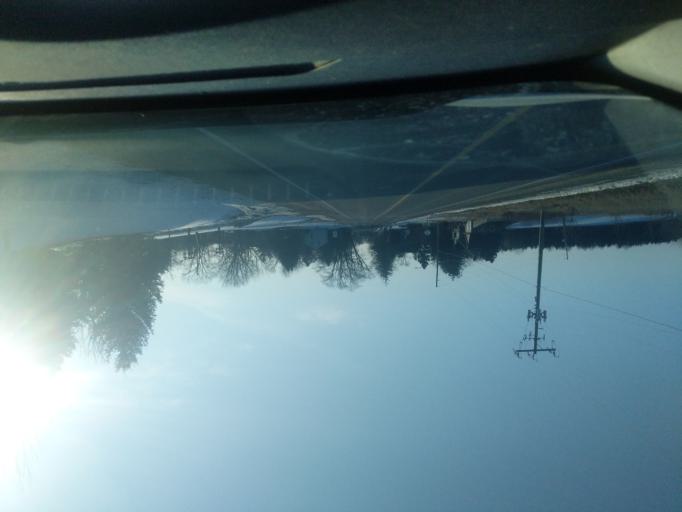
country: CA
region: Ontario
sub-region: Oxford County
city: Woodstock
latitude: 43.2705
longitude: -80.6638
